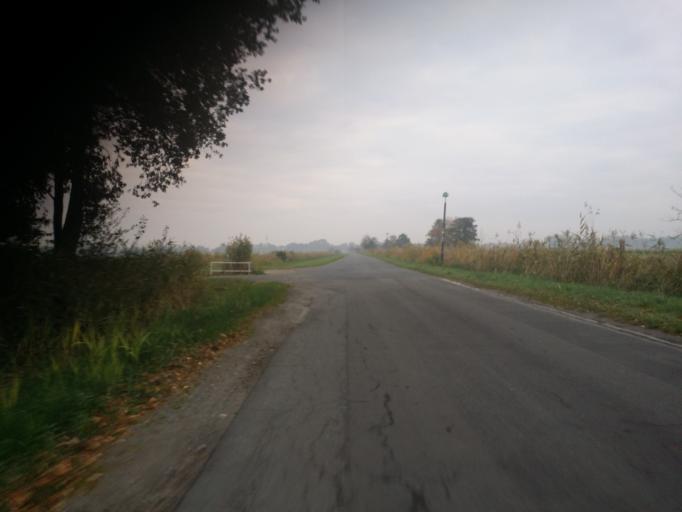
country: DE
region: Bremen
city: Bremen
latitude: 53.1188
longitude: 8.8534
